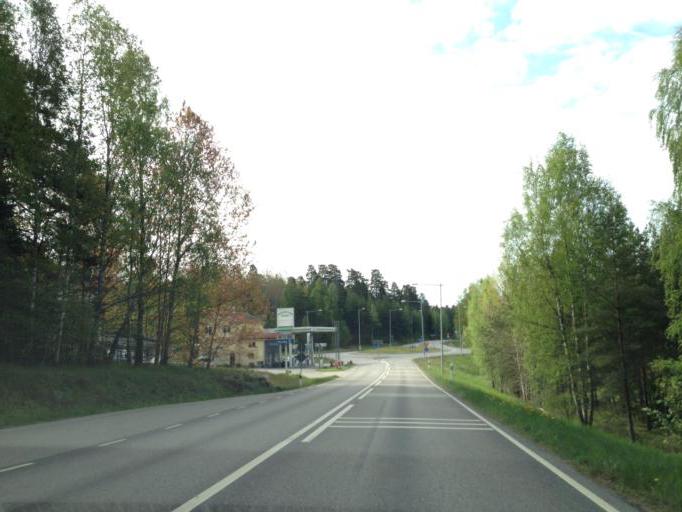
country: SE
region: Soedermanland
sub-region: Flens Kommun
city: Malmkoping
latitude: 59.0682
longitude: 16.8184
